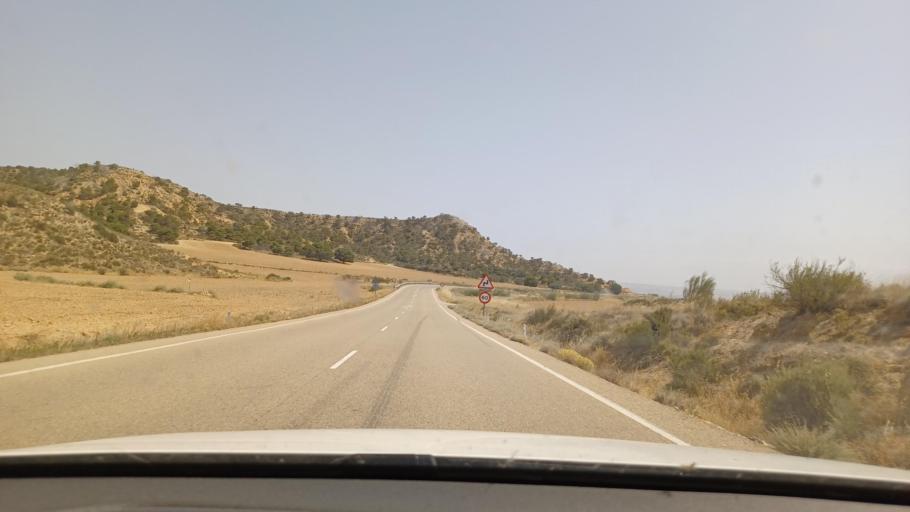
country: ES
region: Aragon
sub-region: Provincia de Zaragoza
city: Chiprana
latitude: 41.3385
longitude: -0.0896
